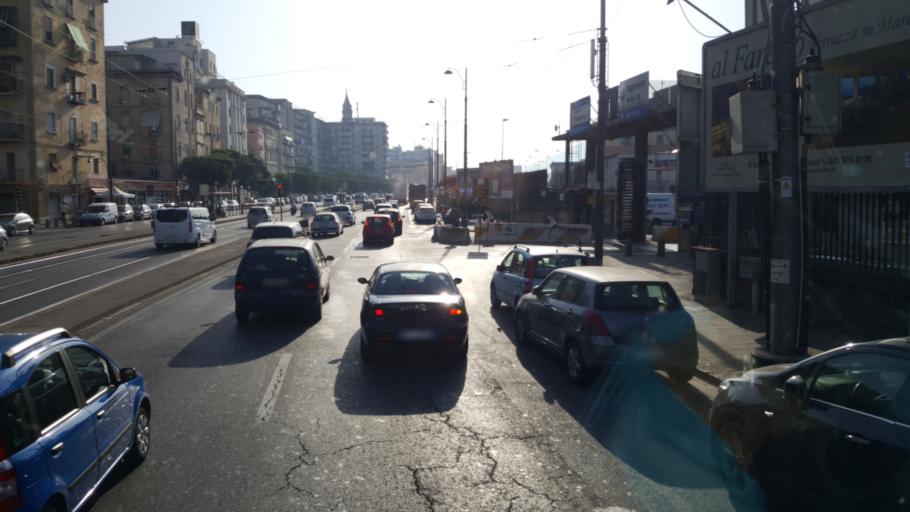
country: IT
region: Campania
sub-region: Provincia di Napoli
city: Napoli
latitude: 40.8454
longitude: 14.2624
